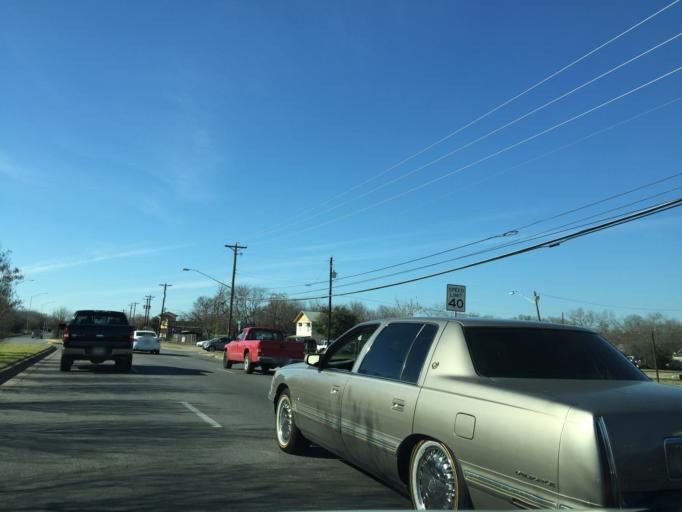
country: US
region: Texas
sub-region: Travis County
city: Austin
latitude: 30.2255
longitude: -97.7043
